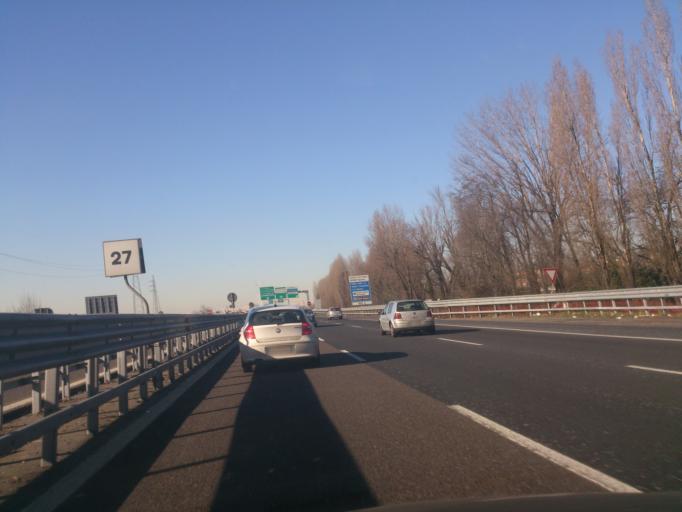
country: IT
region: Lombardy
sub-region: Citta metropolitana di Milano
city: Noverasco-Sporting Mirasole
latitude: 45.3882
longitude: 9.2220
